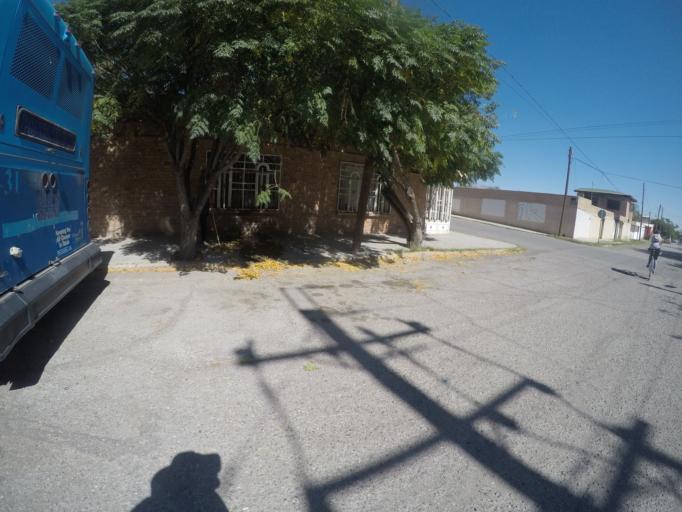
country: MX
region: Chihuahua
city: Ciudad Juarez
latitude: 31.7392
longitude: -106.4700
